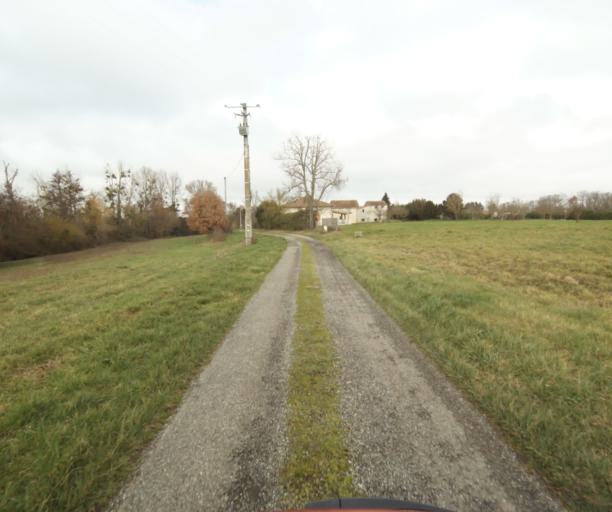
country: FR
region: Languedoc-Roussillon
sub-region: Departement de l'Aude
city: Belpech
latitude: 43.1604
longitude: 1.6948
